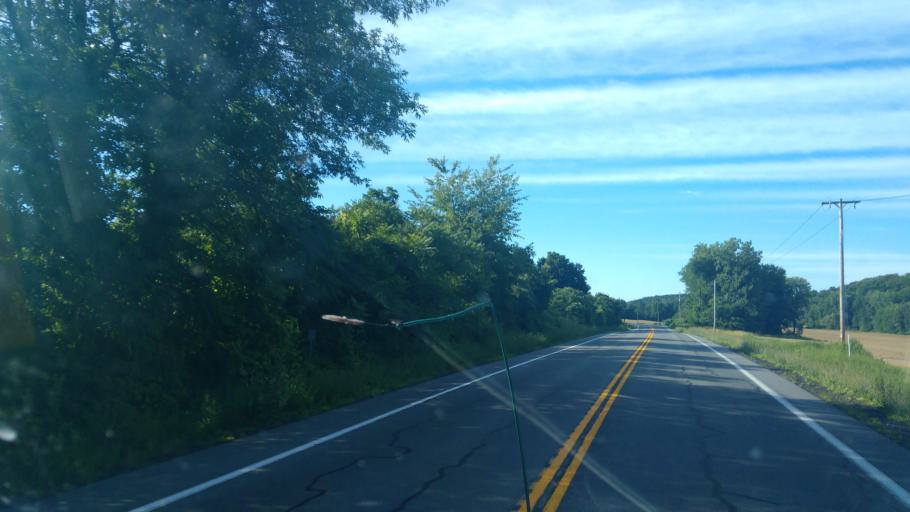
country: US
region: New York
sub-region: Wayne County
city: Lyons
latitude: 43.0954
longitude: -76.9842
